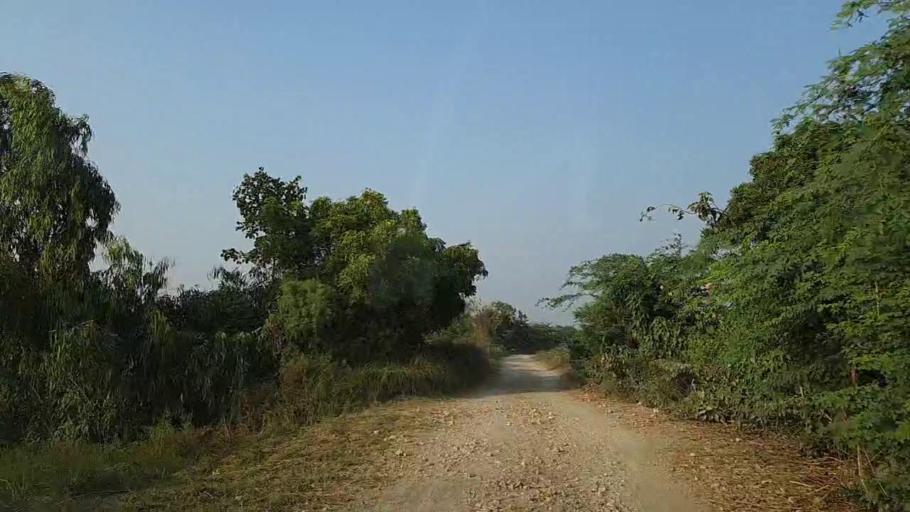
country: PK
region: Sindh
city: Thatta
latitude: 24.6760
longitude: 67.7837
